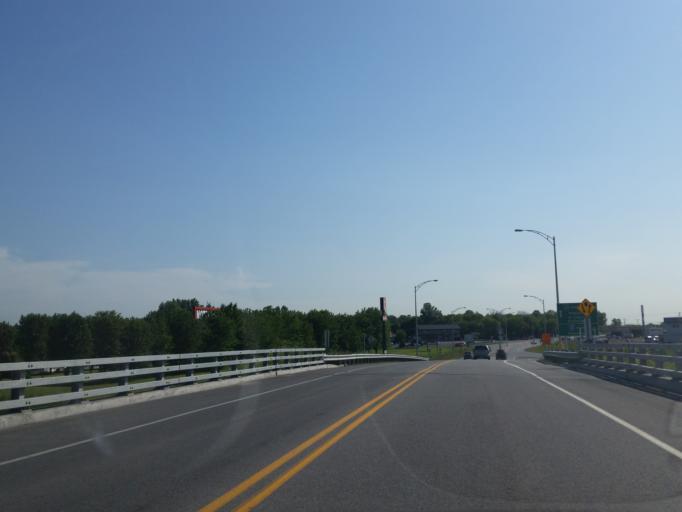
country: CA
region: Quebec
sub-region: Monteregie
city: Napierville
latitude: 45.1934
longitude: -73.4532
